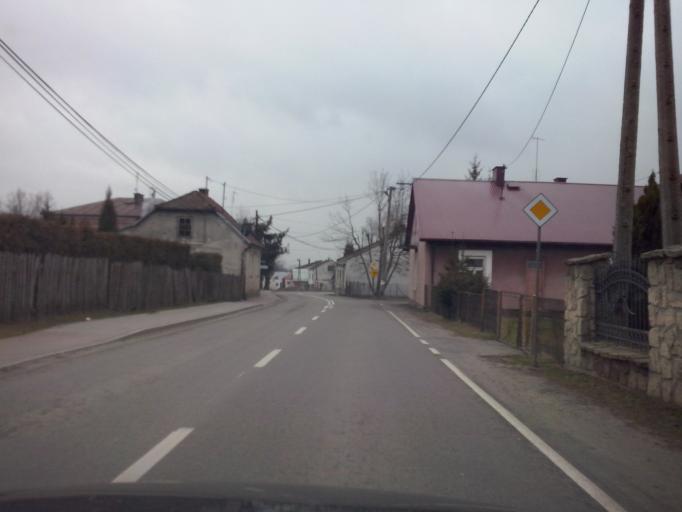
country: PL
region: Subcarpathian Voivodeship
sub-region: Powiat nizanski
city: Krzeszow
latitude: 50.4050
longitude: 22.3414
